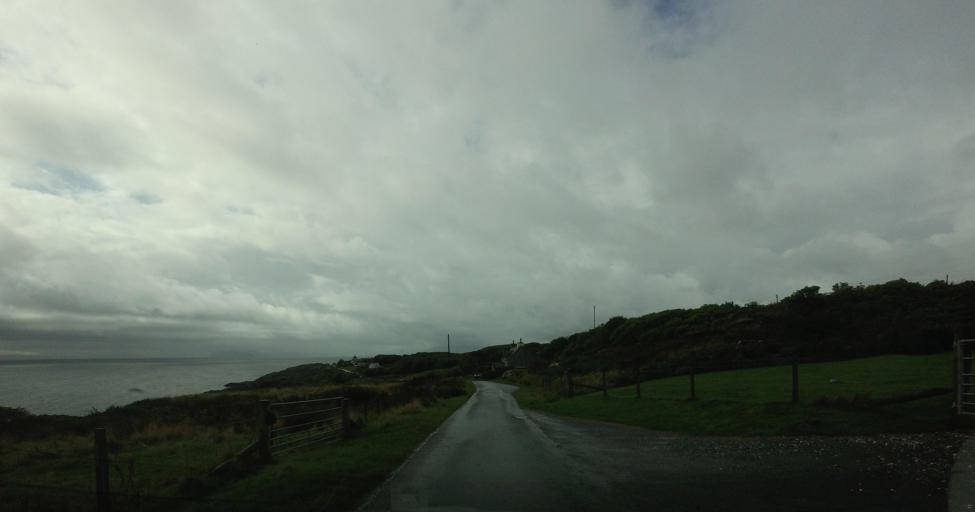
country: GB
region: Scotland
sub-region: Highland
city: Isle of Skye
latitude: 57.1406
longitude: -6.0734
